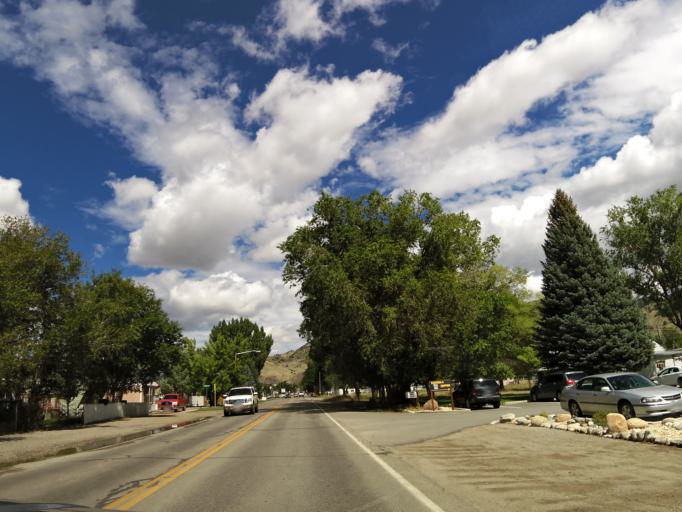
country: US
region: Colorado
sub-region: Chaffee County
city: Salida
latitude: 38.5265
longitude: -105.9847
